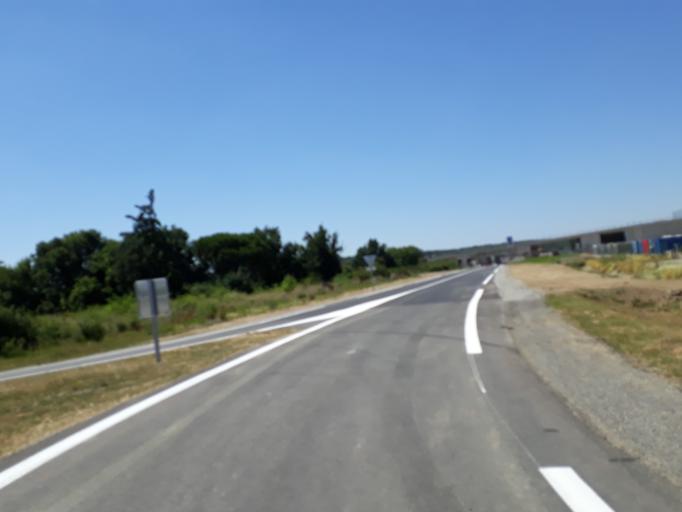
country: FR
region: Midi-Pyrenees
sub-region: Departement de la Haute-Garonne
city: Beauzelle
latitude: 43.6618
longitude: 1.3532
